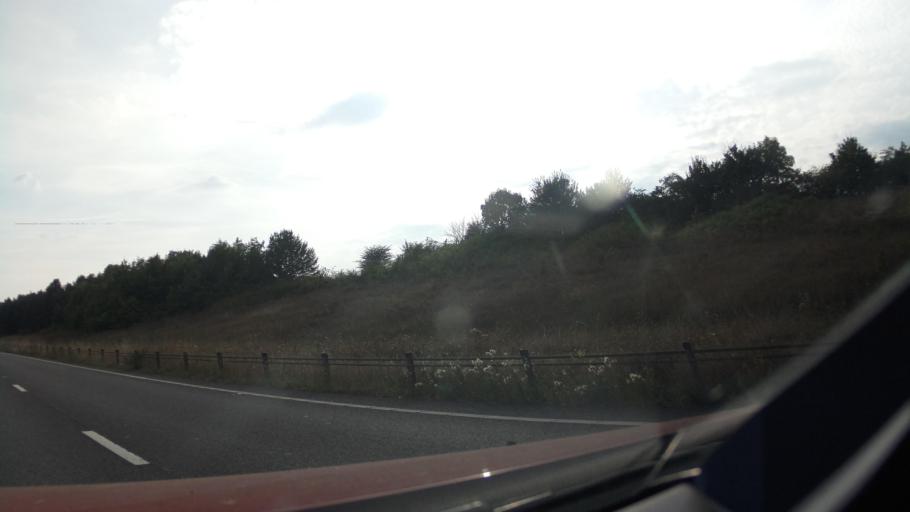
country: GB
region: England
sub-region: Worcestershire
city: Harvington
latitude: 52.1245
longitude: -1.9374
